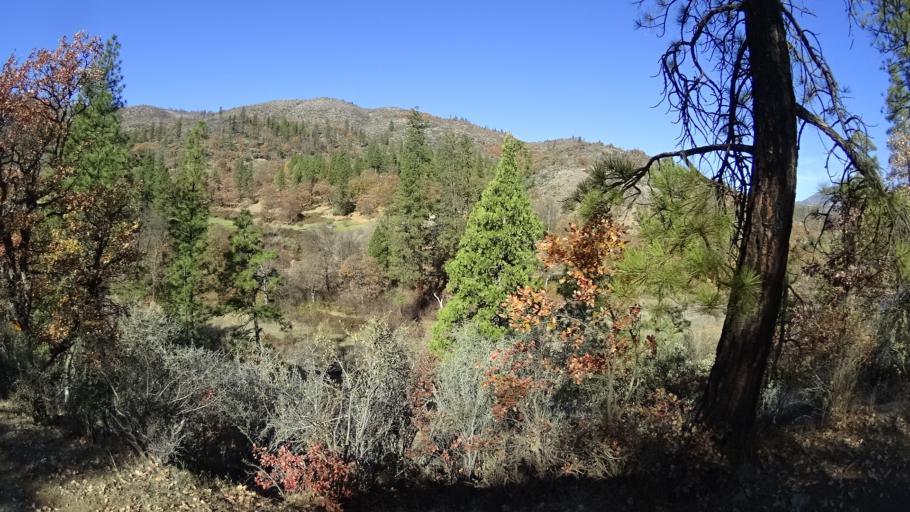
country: US
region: California
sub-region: Siskiyou County
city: Yreka
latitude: 41.8552
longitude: -122.8308
